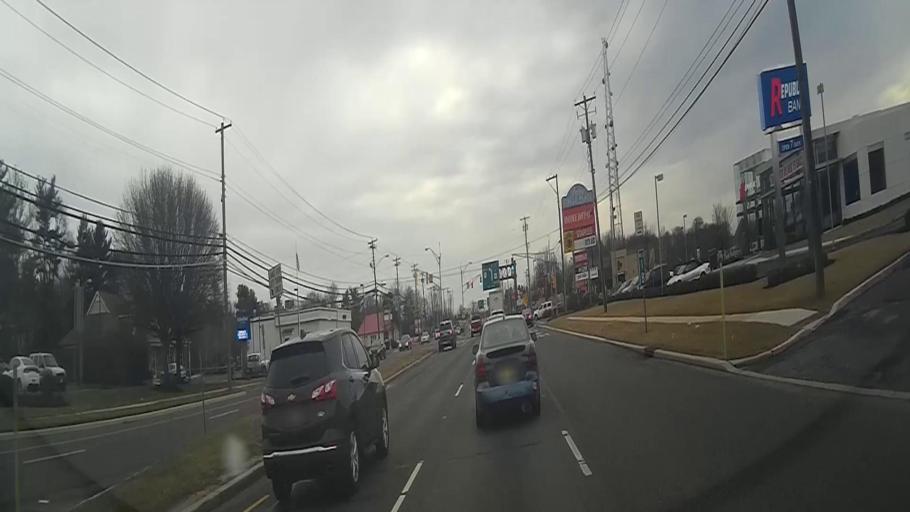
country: US
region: New Jersey
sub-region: Camden County
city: Berlin
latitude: 39.8068
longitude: -74.9314
